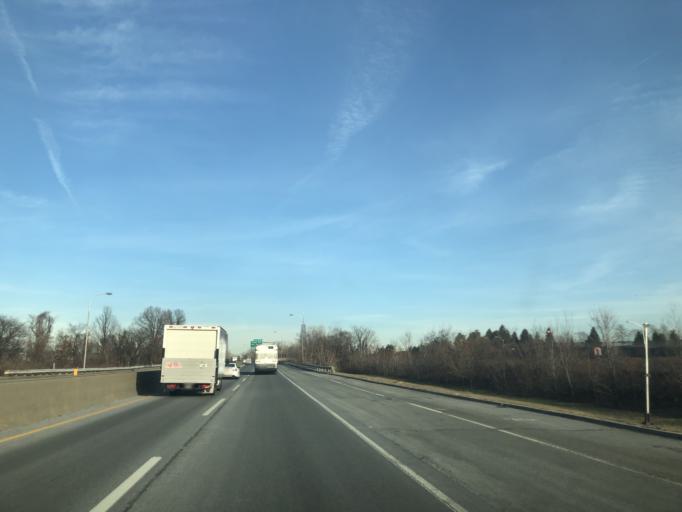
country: US
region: New Jersey
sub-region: Hudson County
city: Jersey City
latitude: 40.6993
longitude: -74.0736
